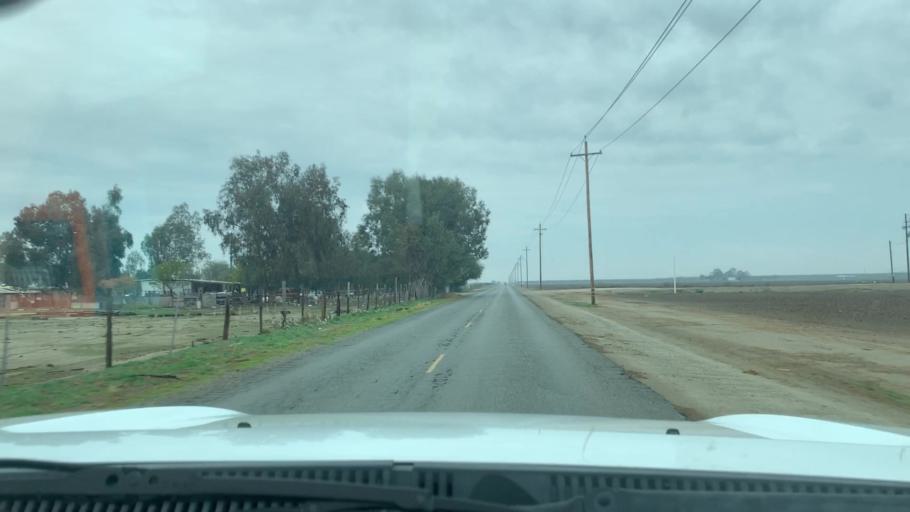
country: US
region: California
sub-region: Tulare County
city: Alpaugh
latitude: 35.7611
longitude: -119.4204
